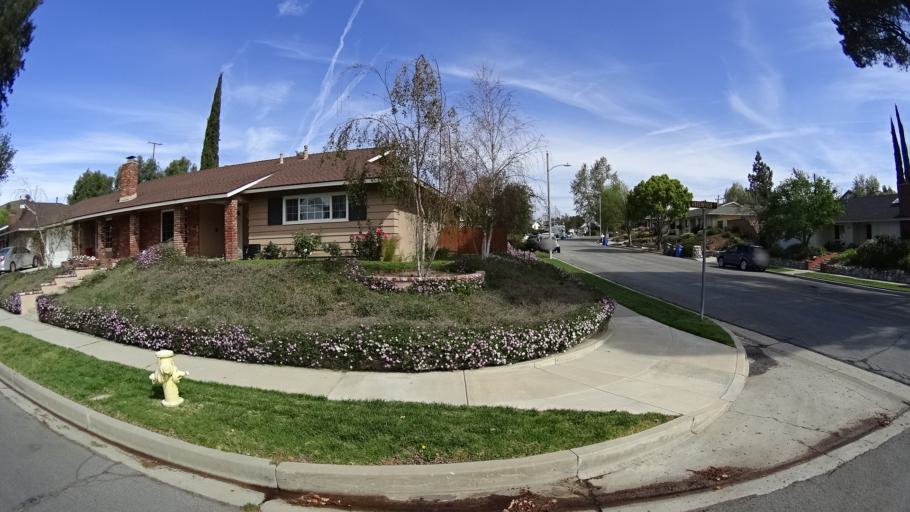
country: US
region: California
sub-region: Ventura County
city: Thousand Oaks
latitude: 34.1947
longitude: -118.8799
